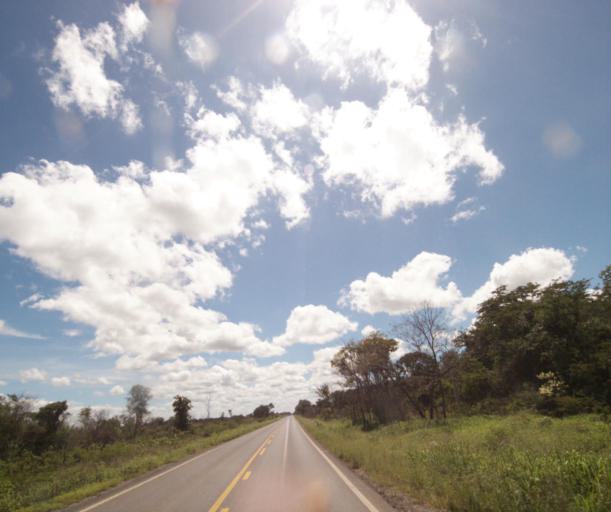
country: BR
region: Bahia
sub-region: Sao Felix Do Coribe
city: Santa Maria da Vitoria
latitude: -13.3944
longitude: -44.1312
